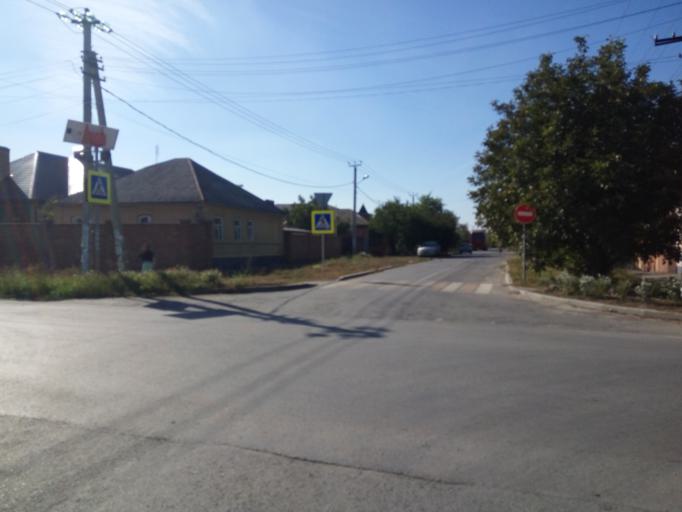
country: RU
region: Rostov
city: Bataysk
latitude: 47.1435
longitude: 39.7357
